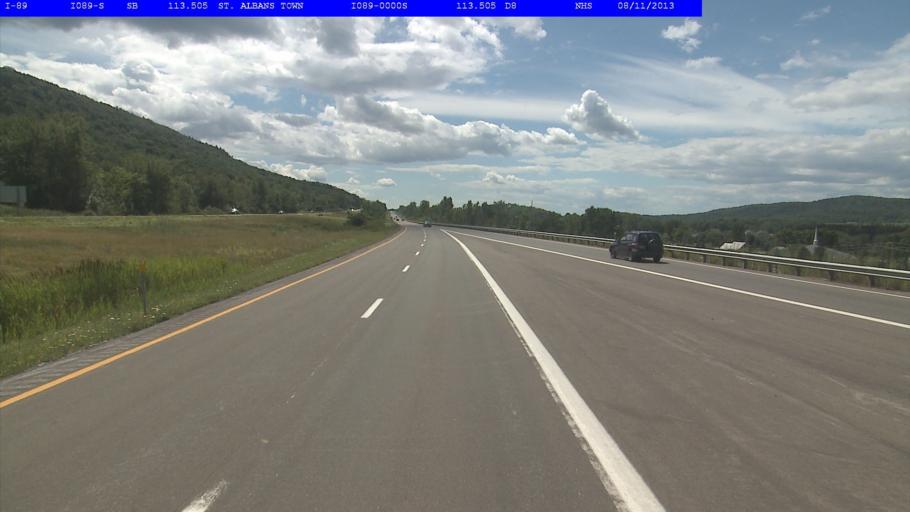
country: US
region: Vermont
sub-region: Franklin County
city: Saint Albans
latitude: 44.7916
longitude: -73.0716
